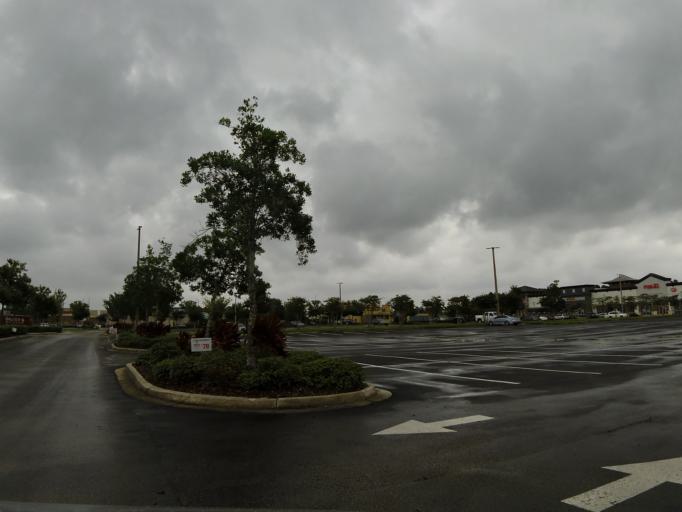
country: US
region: Florida
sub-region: Duval County
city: Jacksonville Beach
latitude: 30.2864
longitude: -81.4612
